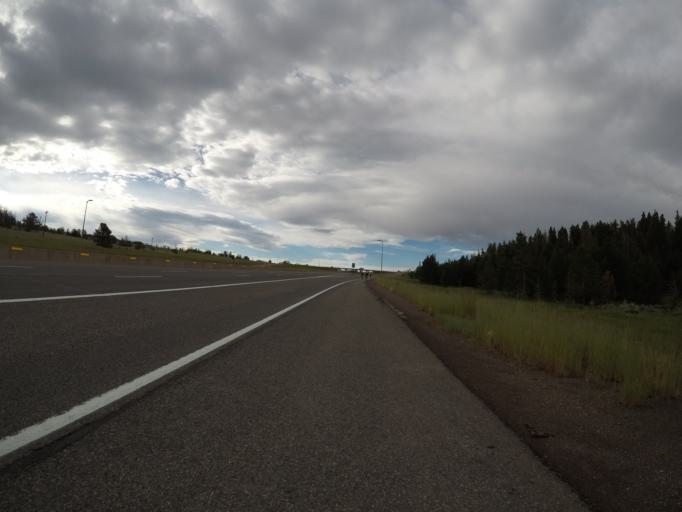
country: US
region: Wyoming
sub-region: Albany County
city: Laramie
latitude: 41.2437
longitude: -105.4404
